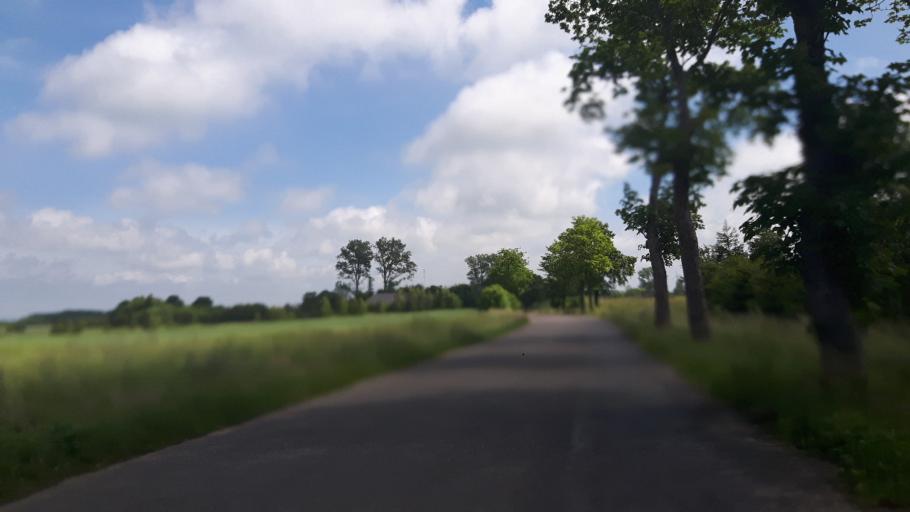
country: PL
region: West Pomeranian Voivodeship
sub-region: Powiat slawienski
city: Slawno
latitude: 54.5086
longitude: 16.6101
